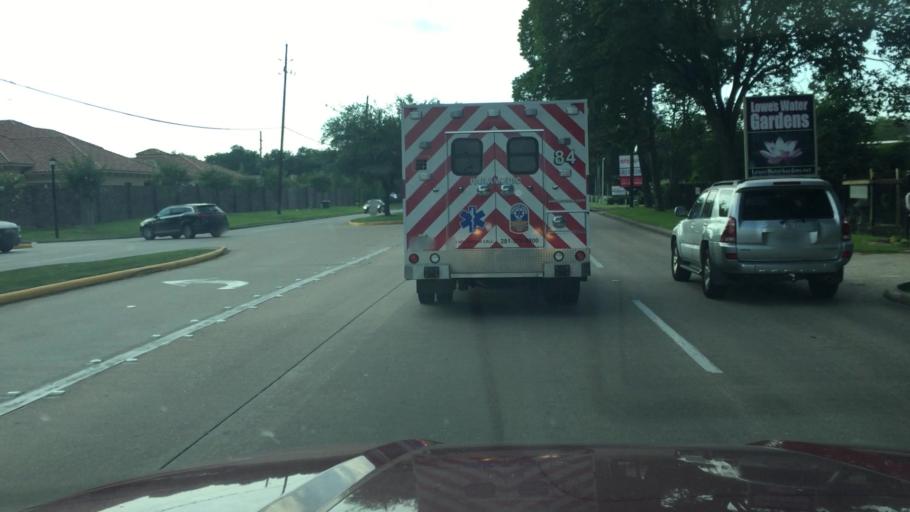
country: US
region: Texas
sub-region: Harris County
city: Tomball
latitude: 30.0243
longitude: -95.5278
